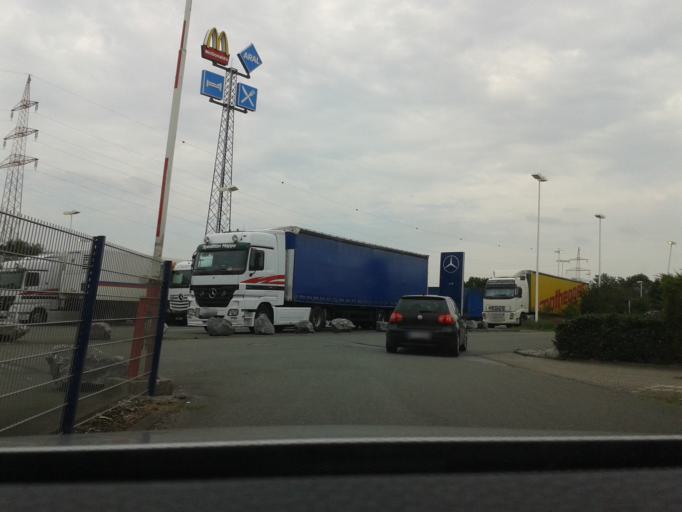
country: DE
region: North Rhine-Westphalia
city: Geseke
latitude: 51.5989
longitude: 8.5158
